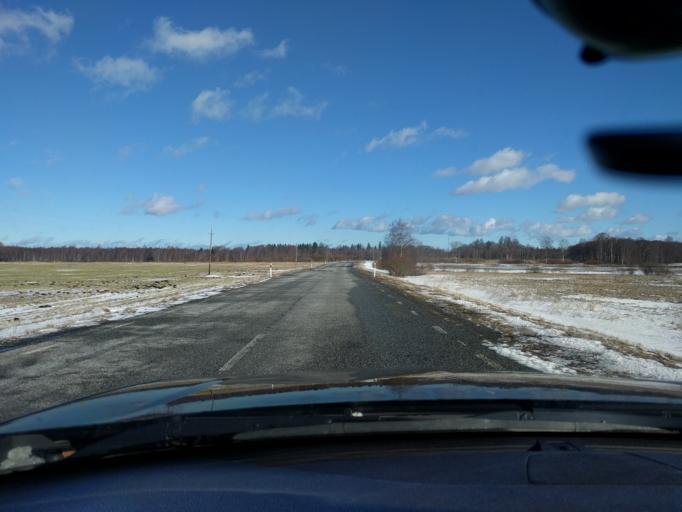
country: EE
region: Harju
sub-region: Raasiku vald
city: Raasiku
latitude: 59.4039
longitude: 25.2048
